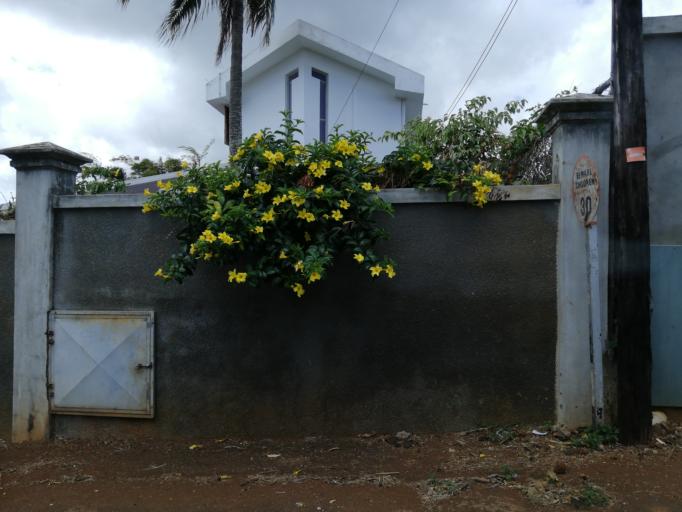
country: MU
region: Moka
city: Moka
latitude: -20.2115
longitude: 57.4738
